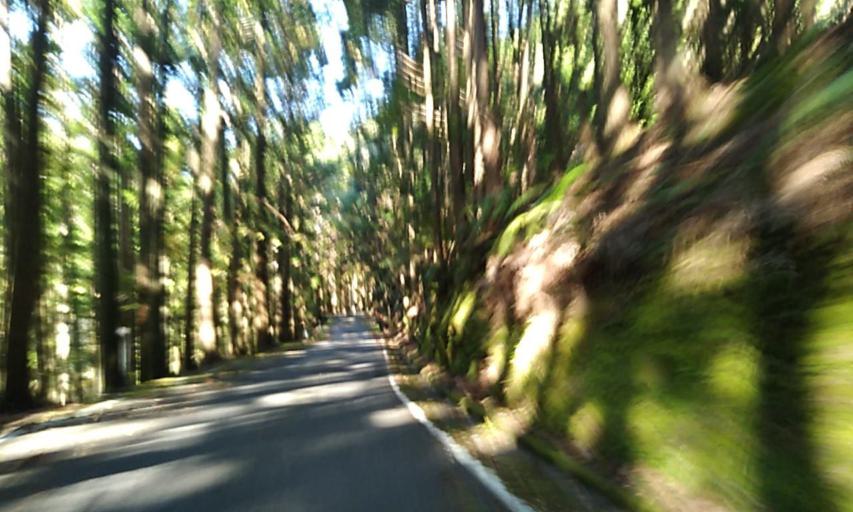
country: JP
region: Wakayama
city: Shingu
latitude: 33.9081
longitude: 136.0010
